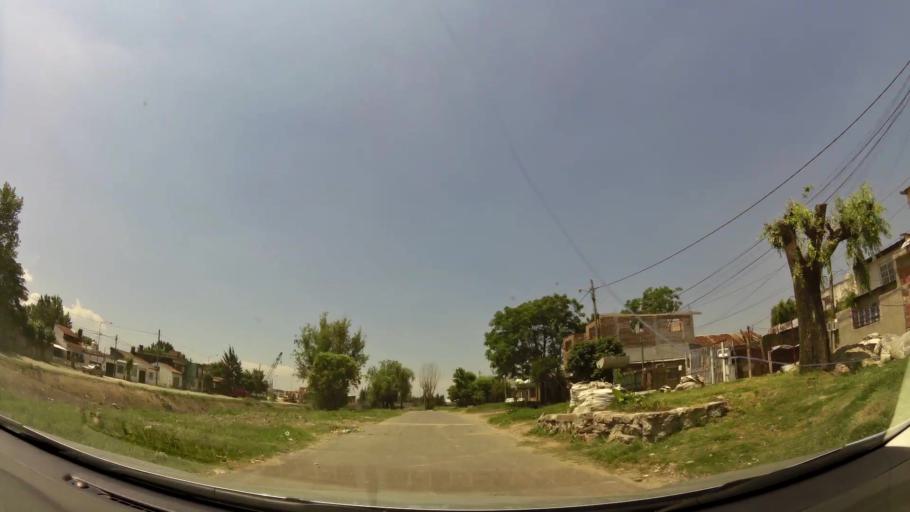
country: AR
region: Buenos Aires
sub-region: Partido de Tigre
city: Tigre
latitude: -34.4501
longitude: -58.5975
